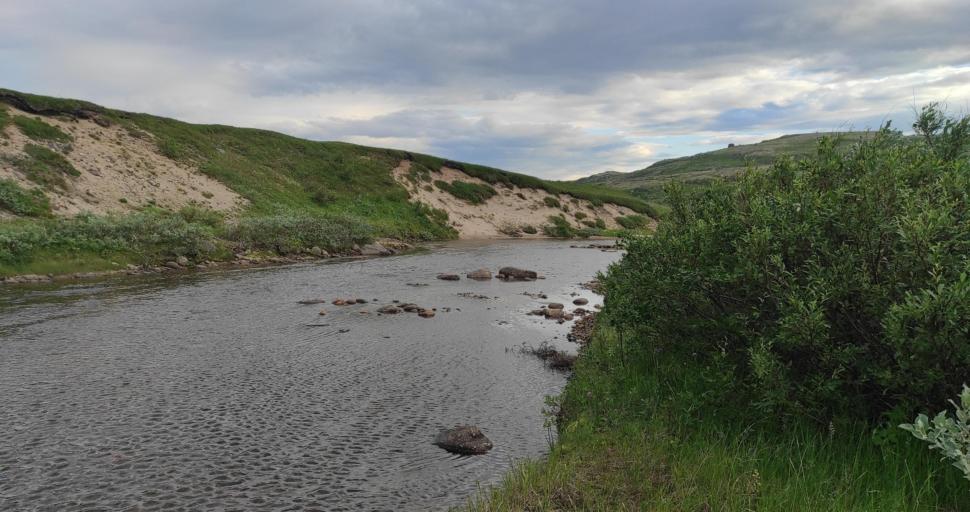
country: RU
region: Murmansk
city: Teriberka
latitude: 69.1863
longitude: 35.6694
